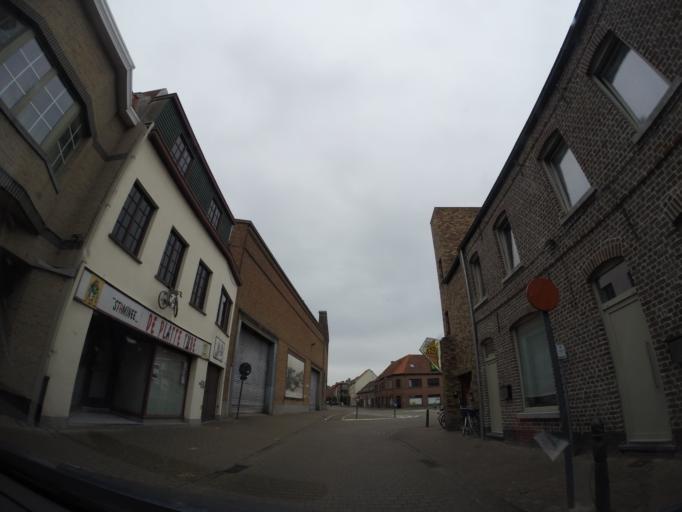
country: BE
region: Flanders
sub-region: Provincie Oost-Vlaanderen
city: Eeklo
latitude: 51.1808
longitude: 3.5685
